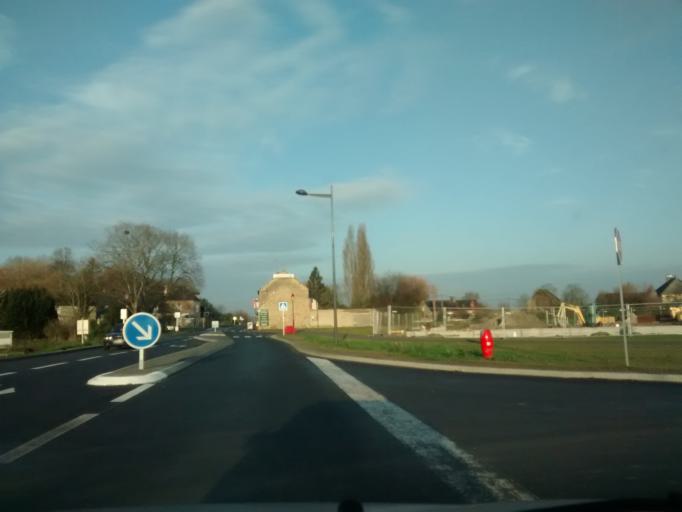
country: FR
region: Lower Normandy
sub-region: Departement de la Manche
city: Pontorson
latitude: 48.5684
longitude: -1.5445
